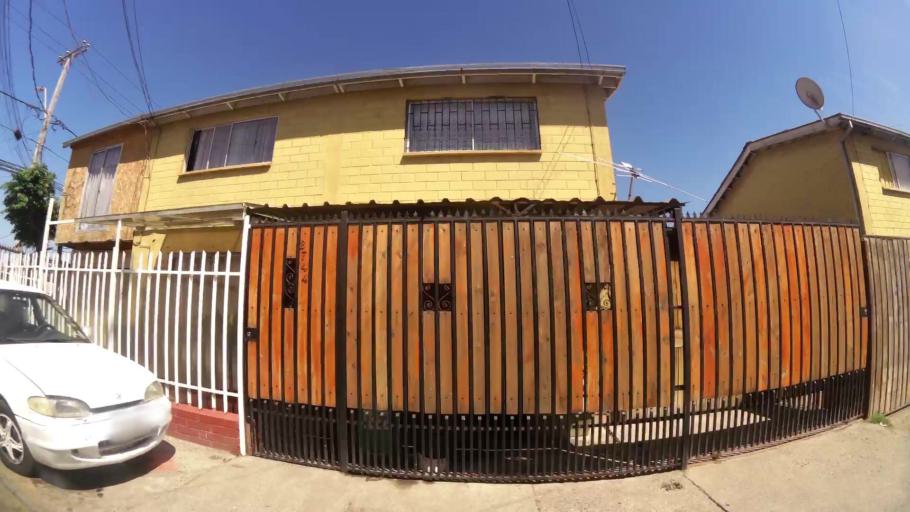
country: CL
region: Santiago Metropolitan
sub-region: Provincia de Maipo
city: San Bernardo
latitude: -33.6244
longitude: -70.6994
